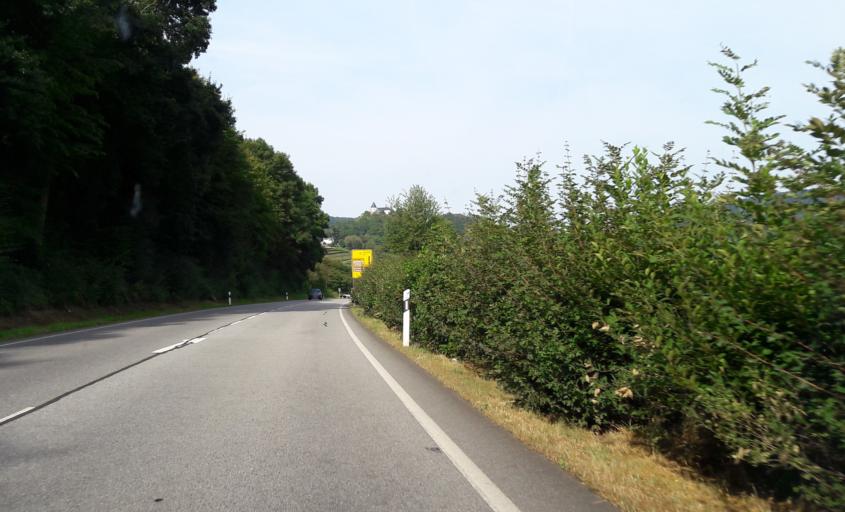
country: DE
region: Rheinland-Pfalz
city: Briedel
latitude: 50.0395
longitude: 7.1548
